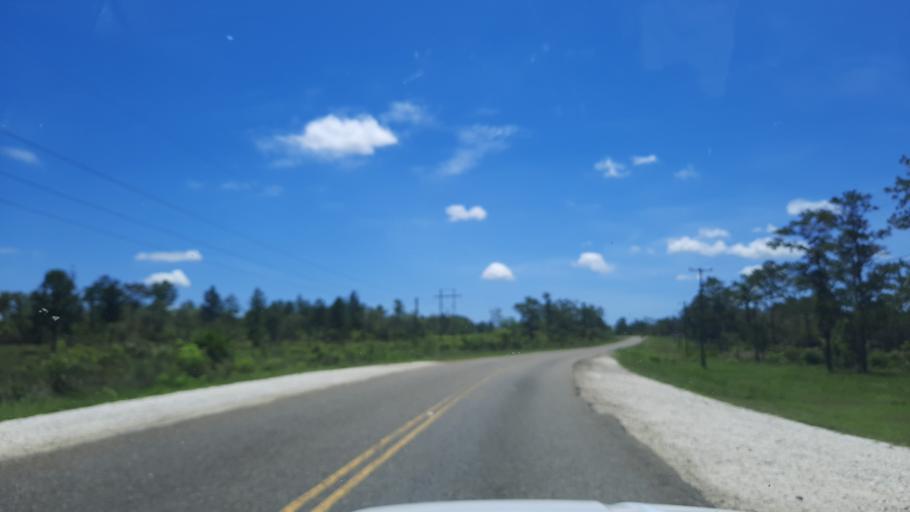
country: BZ
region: Cayo
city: Belmopan
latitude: 17.3331
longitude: -88.5620
